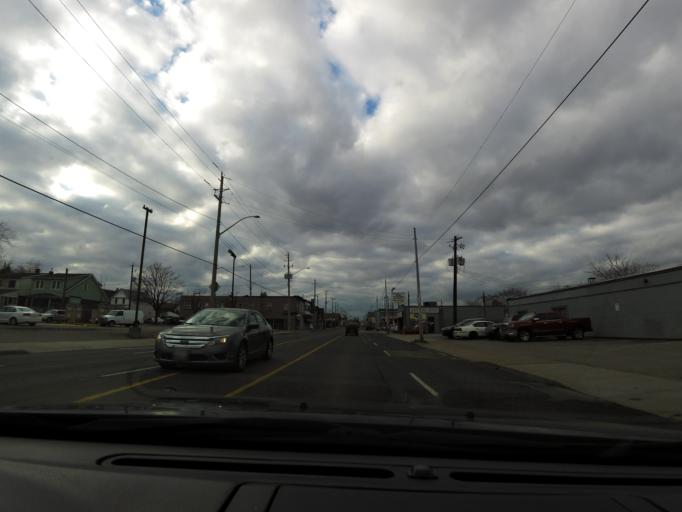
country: CA
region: Ontario
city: Hamilton
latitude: 43.2529
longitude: -79.8220
